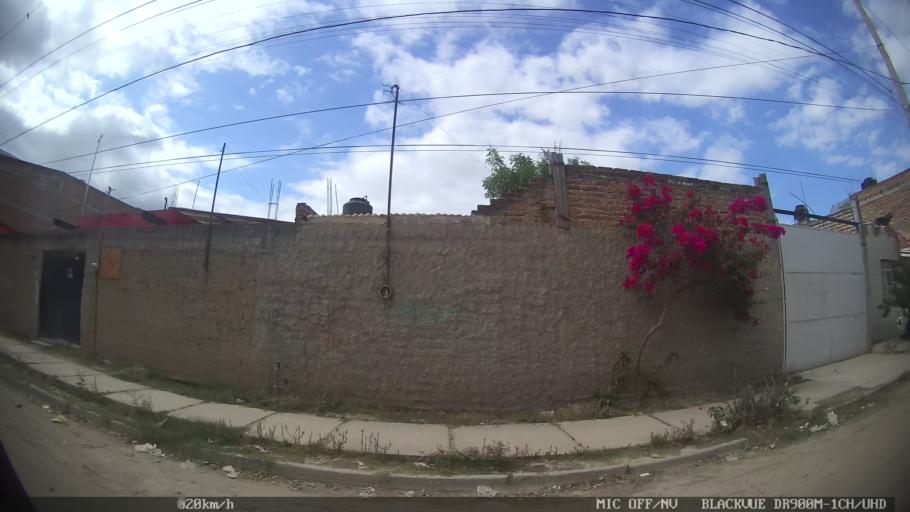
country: MX
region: Jalisco
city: Tlaquepaque
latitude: 20.6701
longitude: -103.2544
